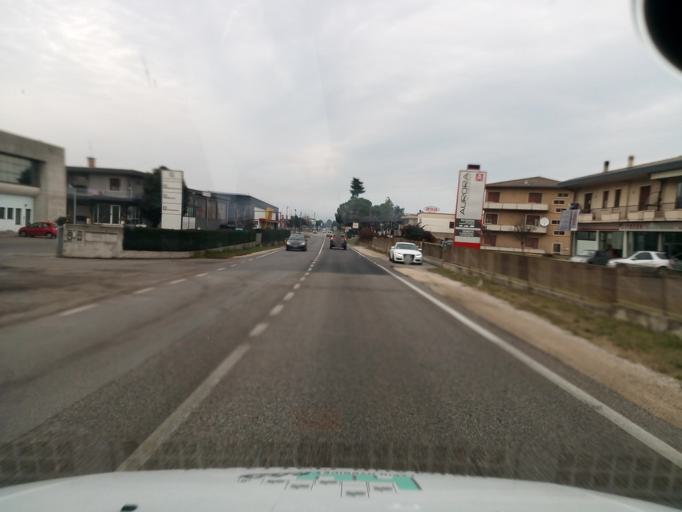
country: IT
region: Veneto
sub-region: Provincia di Vicenza
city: Montebello Vicentino
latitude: 45.4636
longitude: 11.3887
